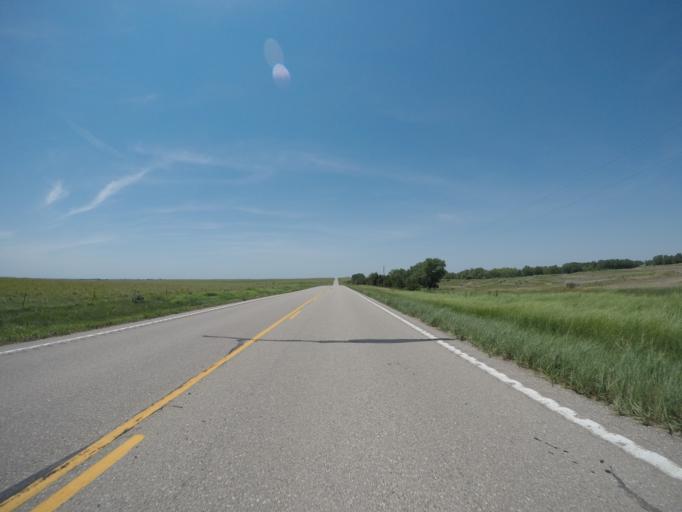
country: US
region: Kansas
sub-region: Dickinson County
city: Solomon
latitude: 39.0307
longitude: -97.4016
